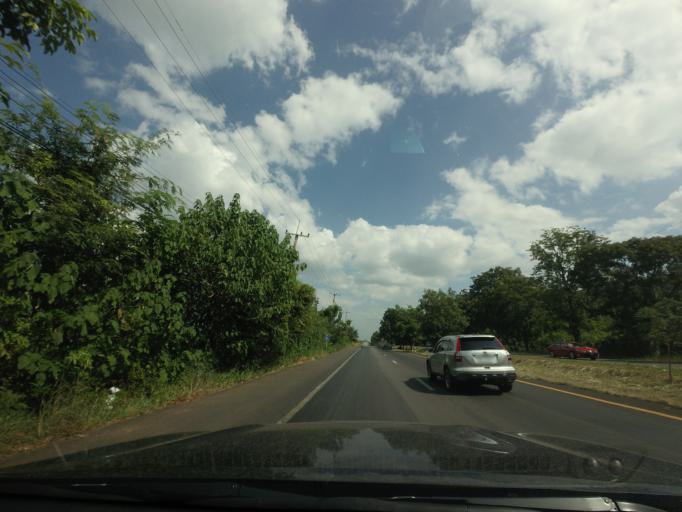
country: TH
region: Phetchabun
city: Wichian Buri
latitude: 15.6280
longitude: 101.0505
